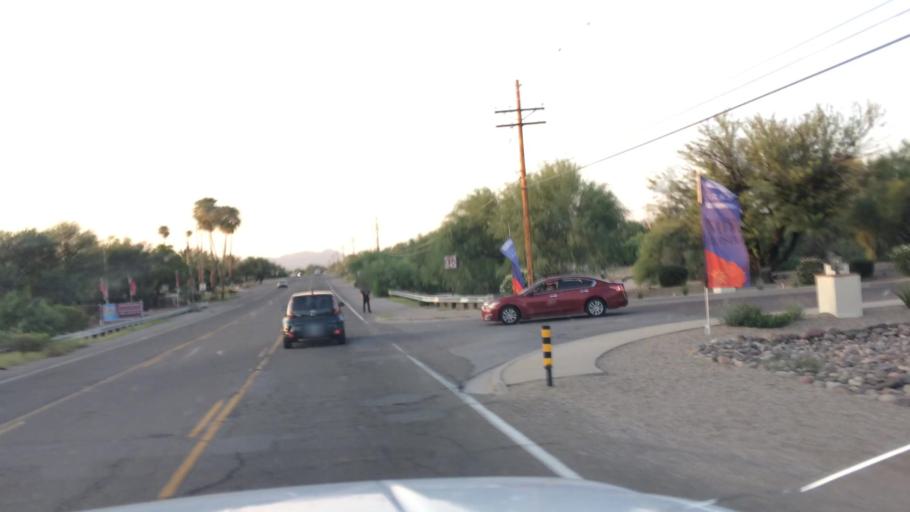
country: US
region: Arizona
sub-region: Pima County
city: Casas Adobes
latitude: 32.3402
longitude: -111.0204
